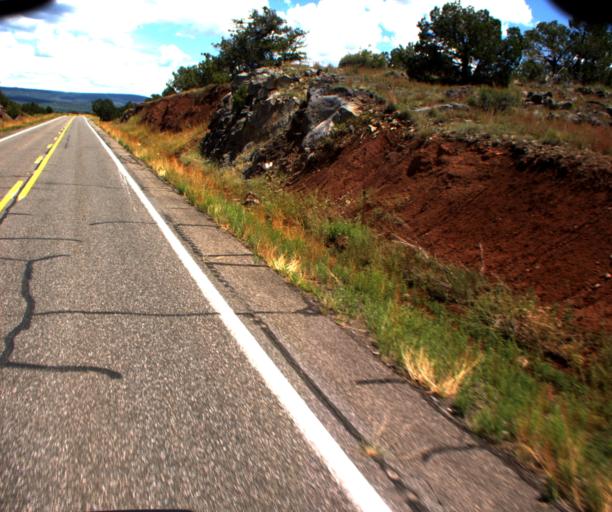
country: US
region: Arizona
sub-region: Gila County
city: Pine
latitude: 34.4860
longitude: -111.6164
